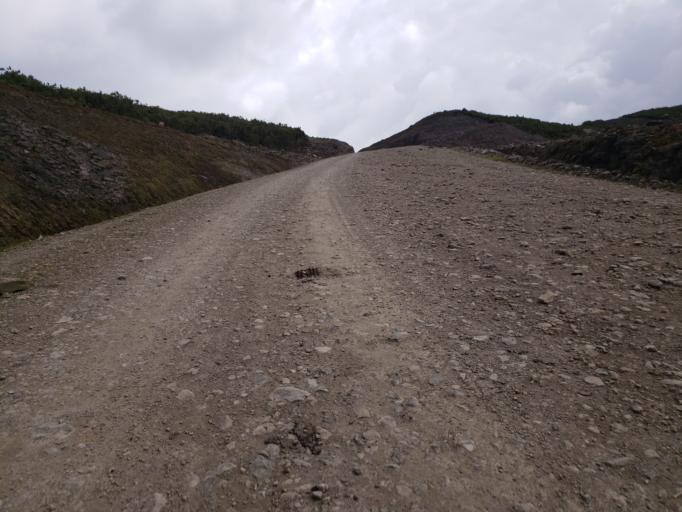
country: ET
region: Oromiya
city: Dodola
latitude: 6.7670
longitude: 39.4222
